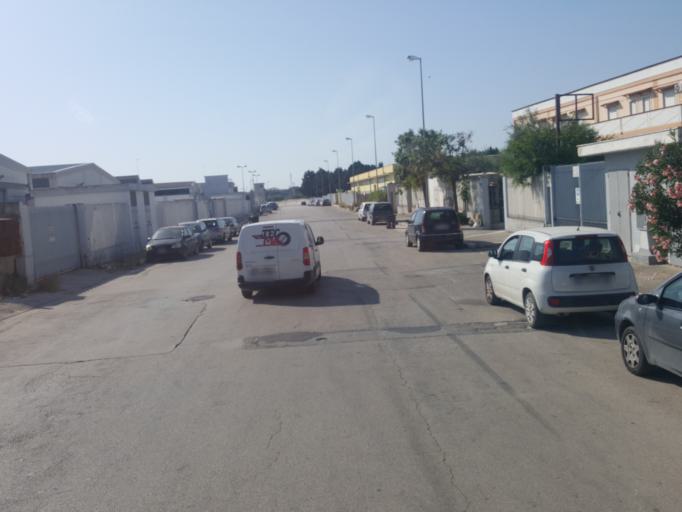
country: IT
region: Apulia
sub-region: Provincia di Barletta - Andria - Trani
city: Barletta
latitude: 41.3094
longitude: 16.3043
